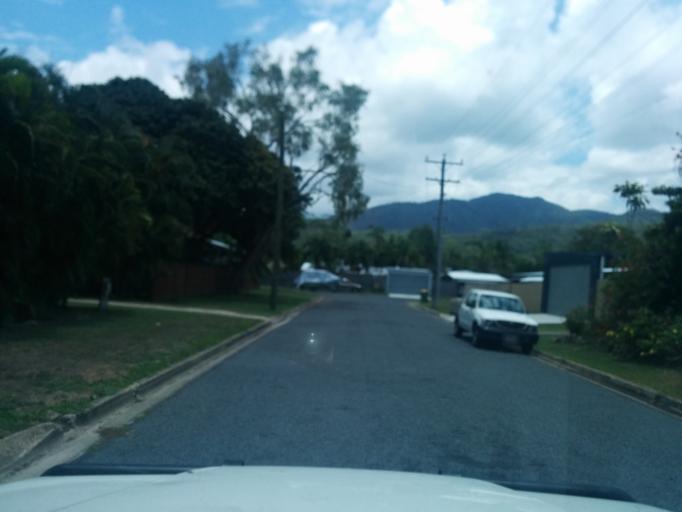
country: AU
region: Queensland
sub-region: Cairns
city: Trinity Beach
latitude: -16.8033
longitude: 145.7007
